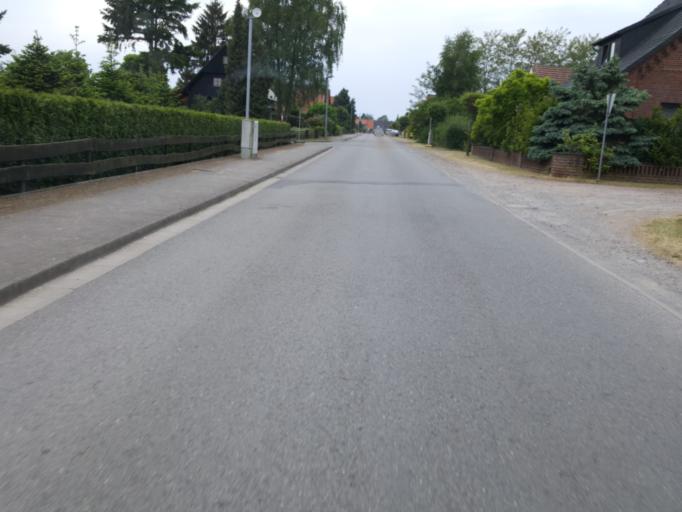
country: DE
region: Lower Saxony
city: Rehburg-Loccum
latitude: 52.4813
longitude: 9.2287
